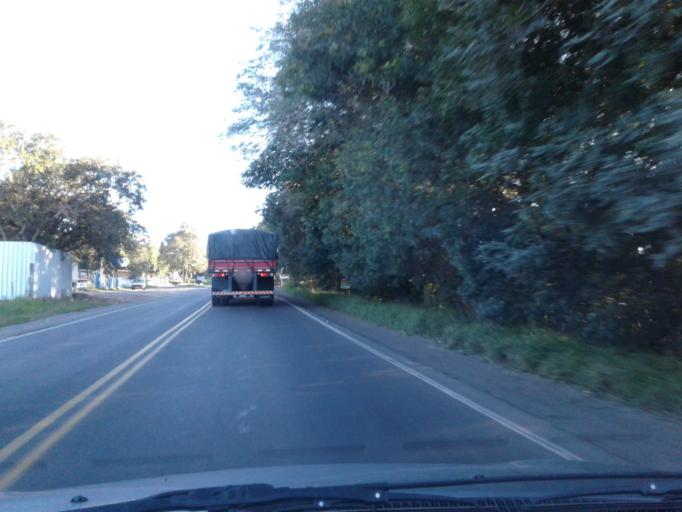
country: BR
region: Rio Grande do Sul
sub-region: Viamao
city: Viamao
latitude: -30.0843
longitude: -51.0195
